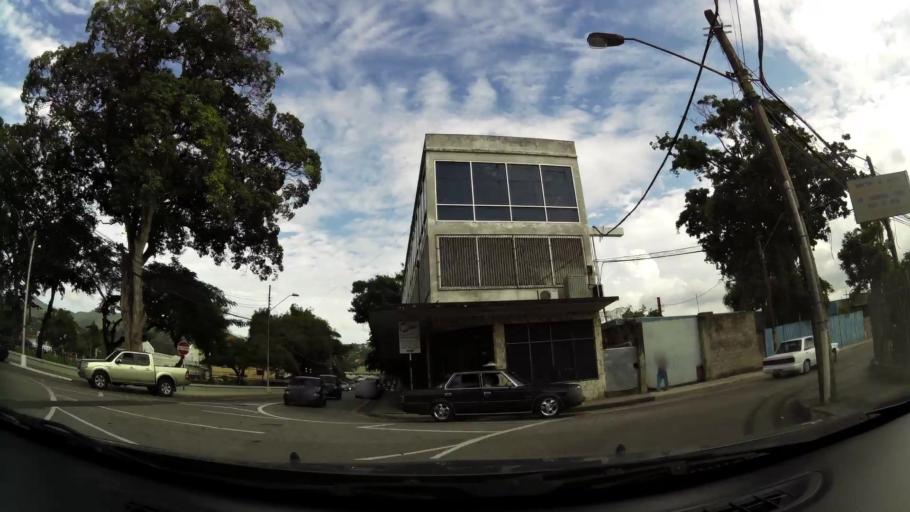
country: TT
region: City of Port of Spain
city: Port-of-Spain
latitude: 10.6626
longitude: -61.5100
